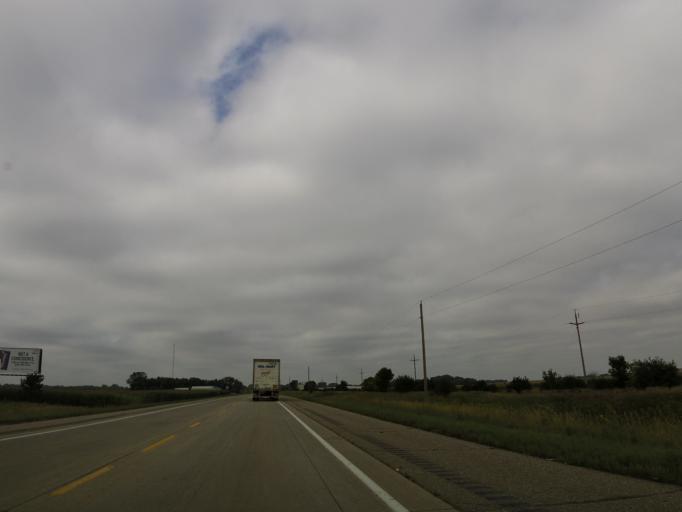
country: US
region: Minnesota
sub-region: Renville County
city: Olivia
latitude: 44.7748
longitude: -94.9613
